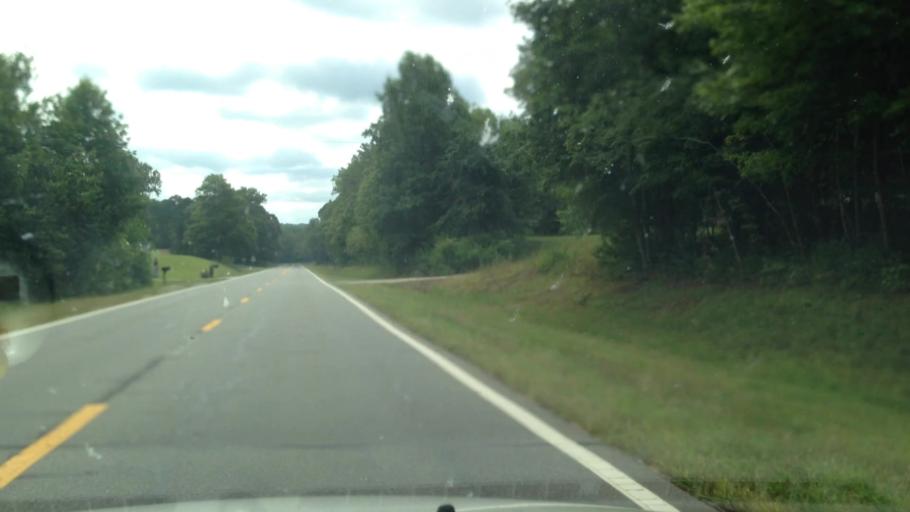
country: US
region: North Carolina
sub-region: Rockingham County
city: Madison
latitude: 36.3799
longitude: -79.8910
